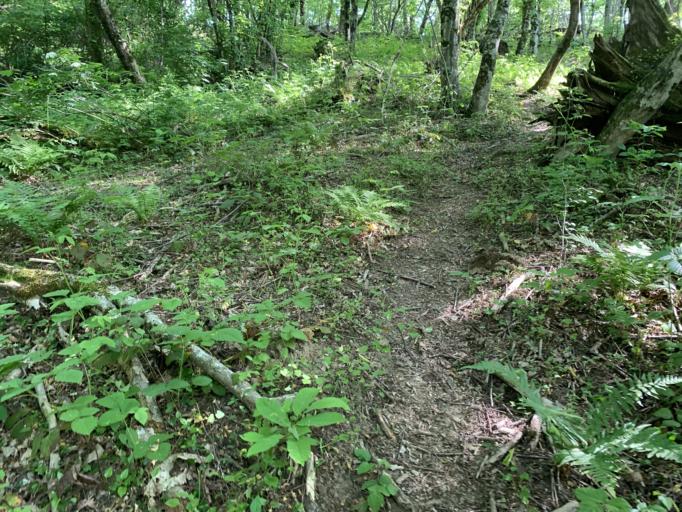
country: RU
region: Krasnodarskiy
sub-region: Sochi City
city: Lazarevskoye
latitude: 43.9510
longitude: 39.3230
